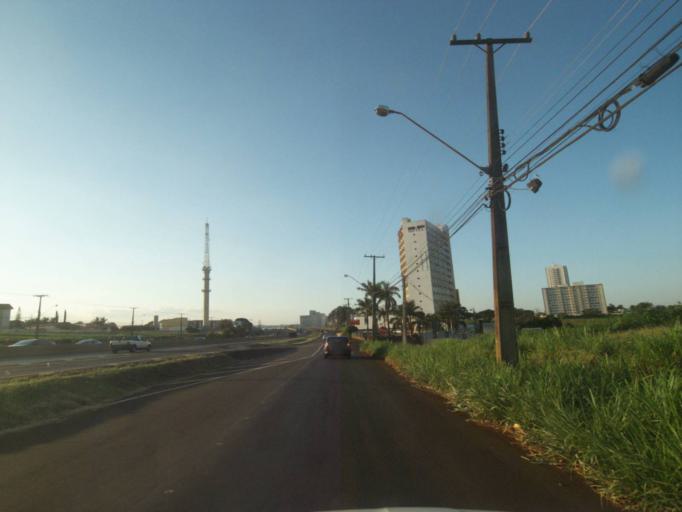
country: BR
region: Parana
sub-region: Londrina
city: Londrina
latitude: -23.3272
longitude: -51.1892
